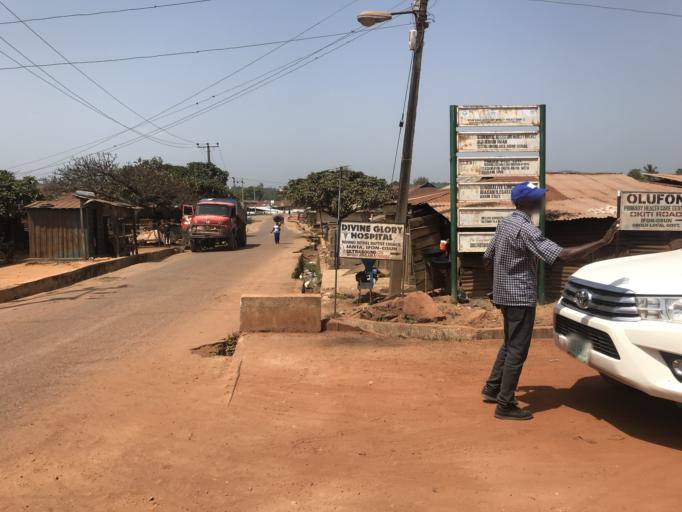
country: NG
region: Osun
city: Ifon
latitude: 7.8637
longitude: 4.4758
